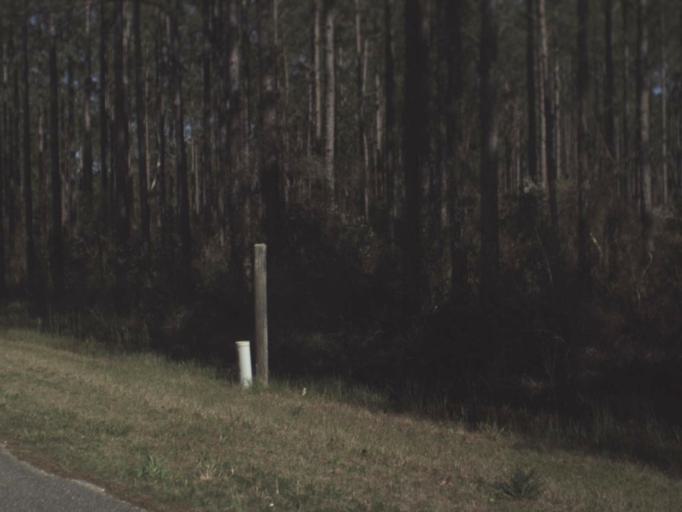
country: US
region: Florida
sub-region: Gulf County
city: Port Saint Joe
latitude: 29.8391
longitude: -85.2711
